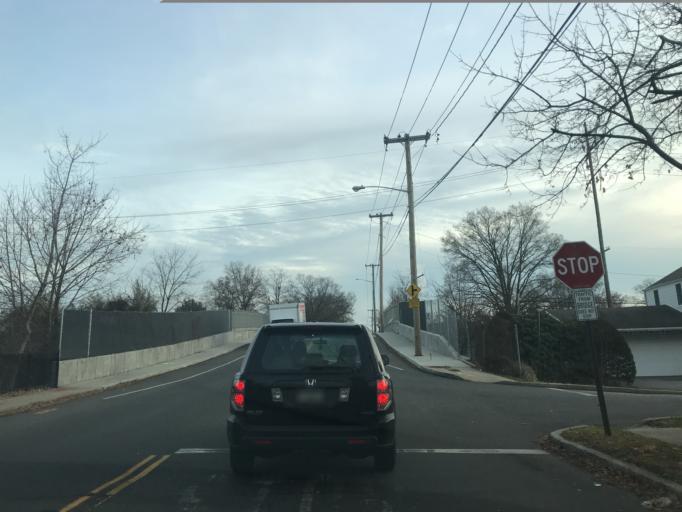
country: US
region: New York
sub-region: Nassau County
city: Westbury
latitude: 40.7521
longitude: -73.5960
